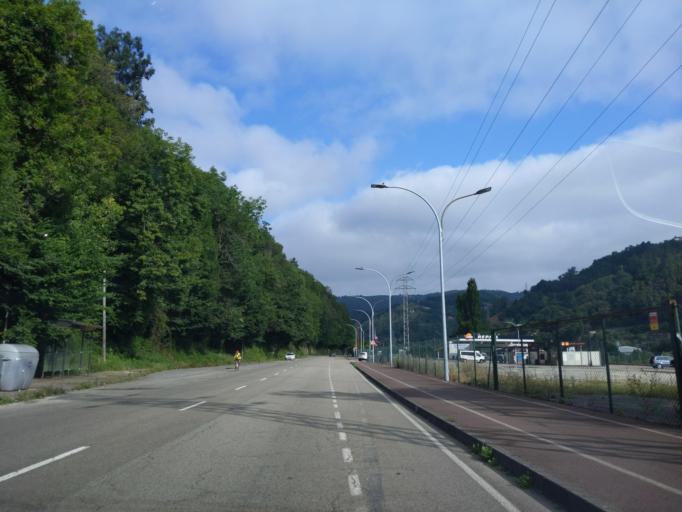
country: ES
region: Asturias
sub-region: Province of Asturias
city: El entrego
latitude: 43.2761
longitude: -5.6170
